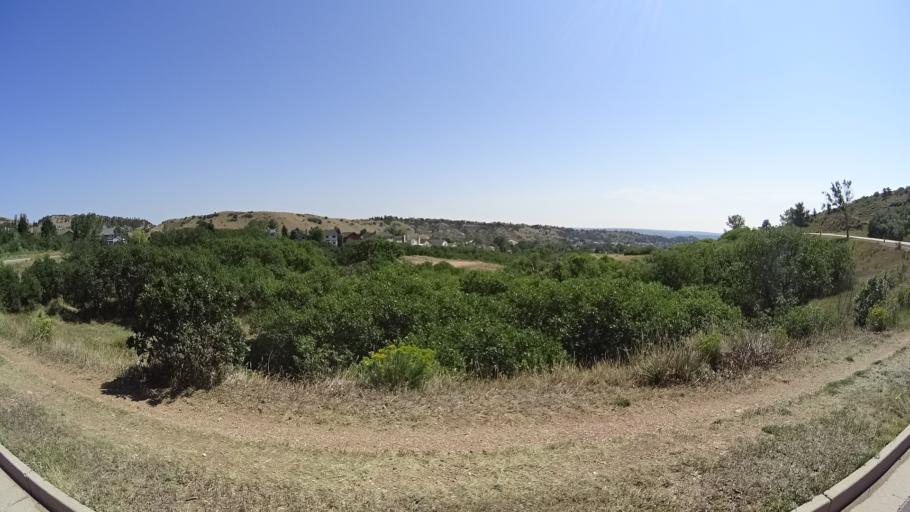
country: US
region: Colorado
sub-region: El Paso County
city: Air Force Academy
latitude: 38.9346
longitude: -104.8809
